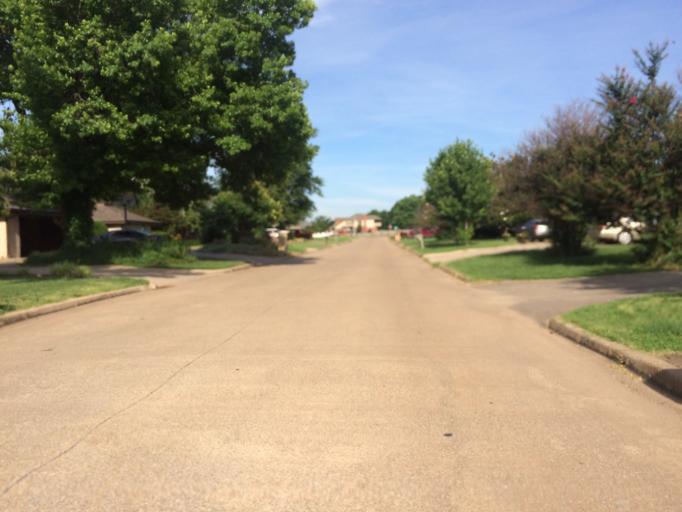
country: US
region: Oklahoma
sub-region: Cleveland County
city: Norman
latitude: 35.2277
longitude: -97.4745
